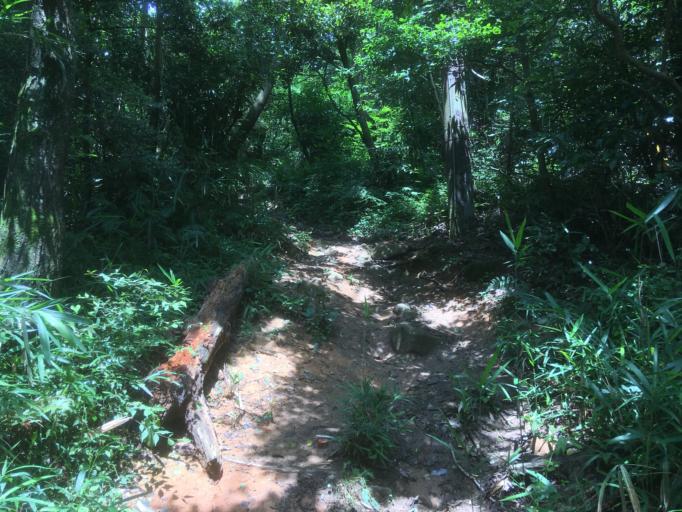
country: JP
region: Nara
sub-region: Ikoma-shi
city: Ikoma
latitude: 34.6735
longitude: 135.6762
